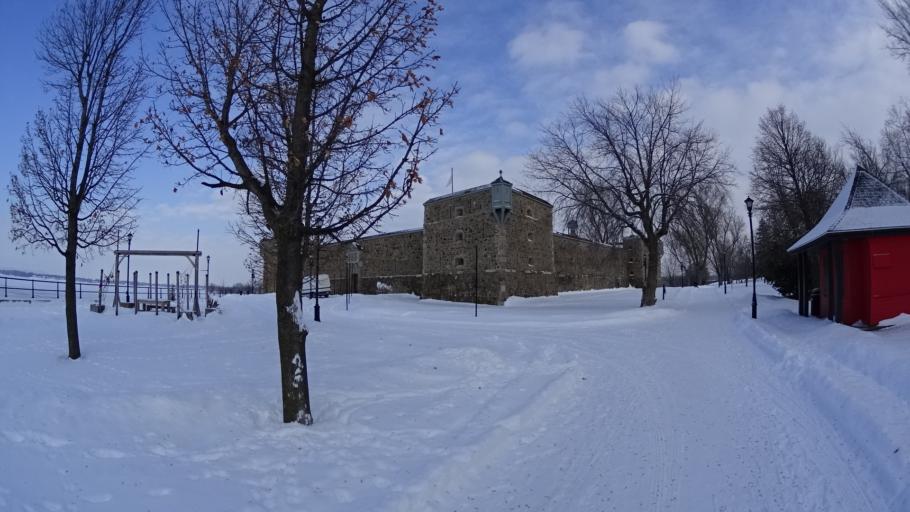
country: CA
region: Quebec
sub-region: Monteregie
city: Chambly
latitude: 45.4491
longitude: -73.2775
